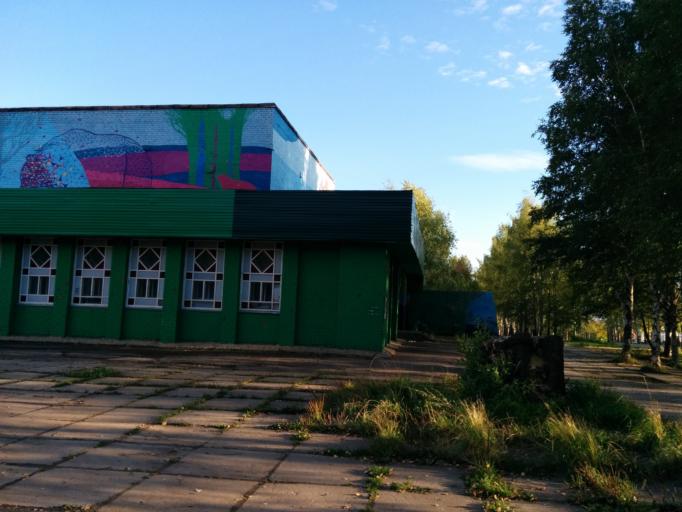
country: RU
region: Perm
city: Kudymkar
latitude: 59.0146
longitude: 54.6677
